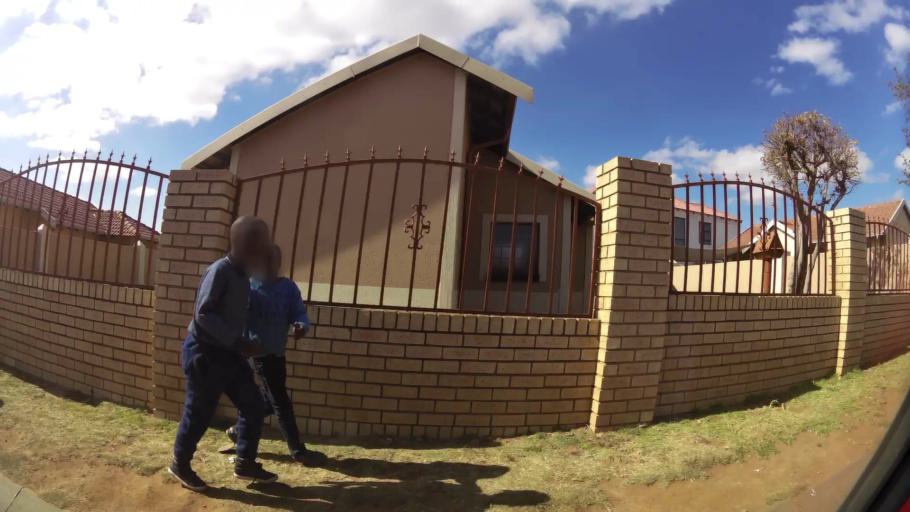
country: ZA
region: Gauteng
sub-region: City of Johannesburg Metropolitan Municipality
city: Modderfontein
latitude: -26.0307
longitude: 28.1764
